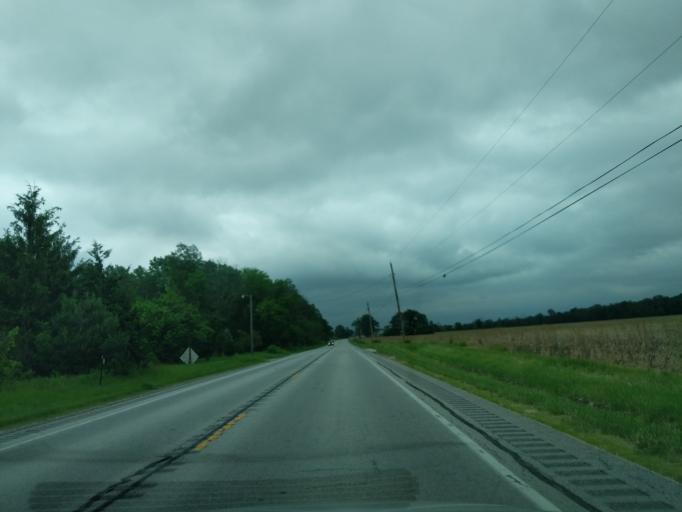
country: US
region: Indiana
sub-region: Madison County
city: Frankton
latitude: 40.2775
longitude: -85.7437
